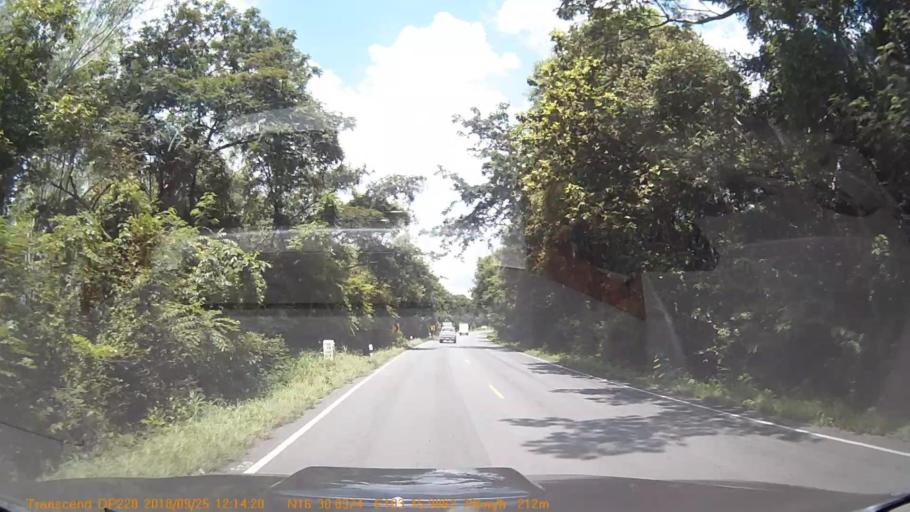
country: TH
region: Kalasin
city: Huai Mek
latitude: 16.5141
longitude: 103.2666
